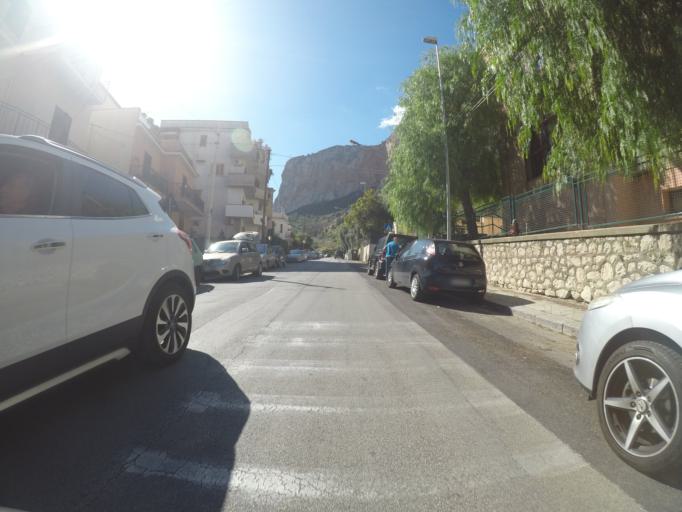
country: IT
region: Sicily
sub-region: Palermo
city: Palermo
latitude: 38.1666
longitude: 13.3659
